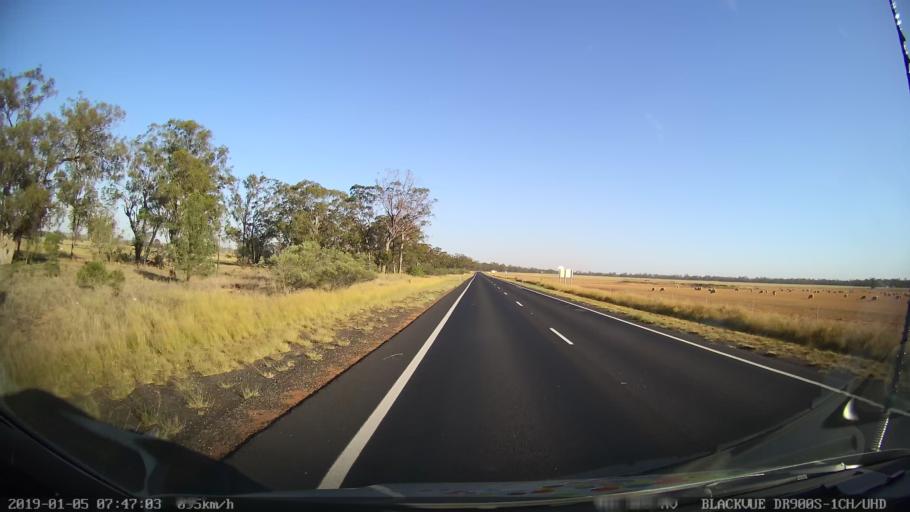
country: AU
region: New South Wales
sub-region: Gilgandra
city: Gilgandra
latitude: -31.8357
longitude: 148.6407
